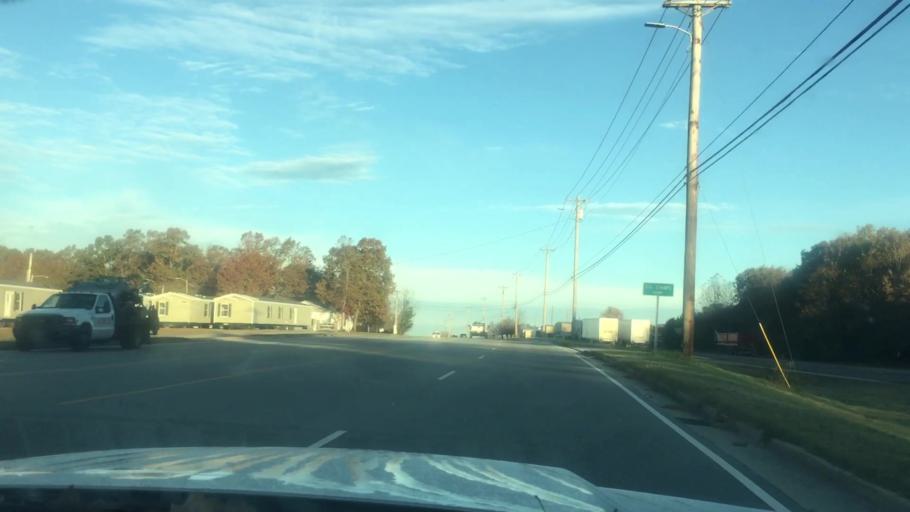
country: US
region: Tennessee
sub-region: Coffee County
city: Tullahoma
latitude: 35.3447
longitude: -86.1942
